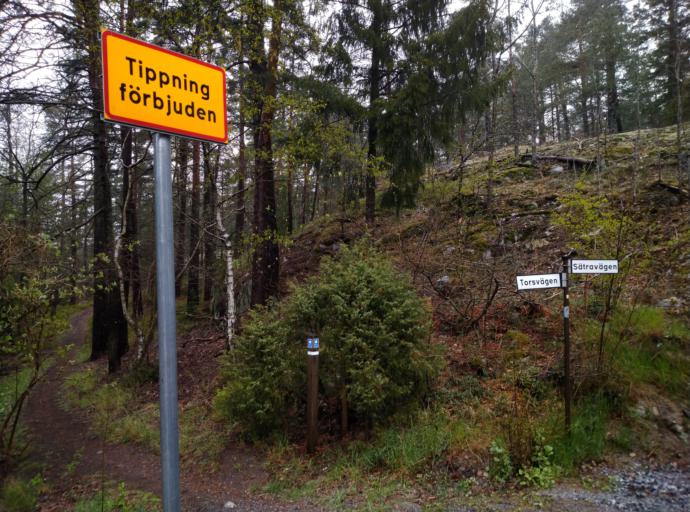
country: SE
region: Stockholm
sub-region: Nacka Kommun
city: Fisksatra
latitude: 59.2930
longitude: 18.2719
